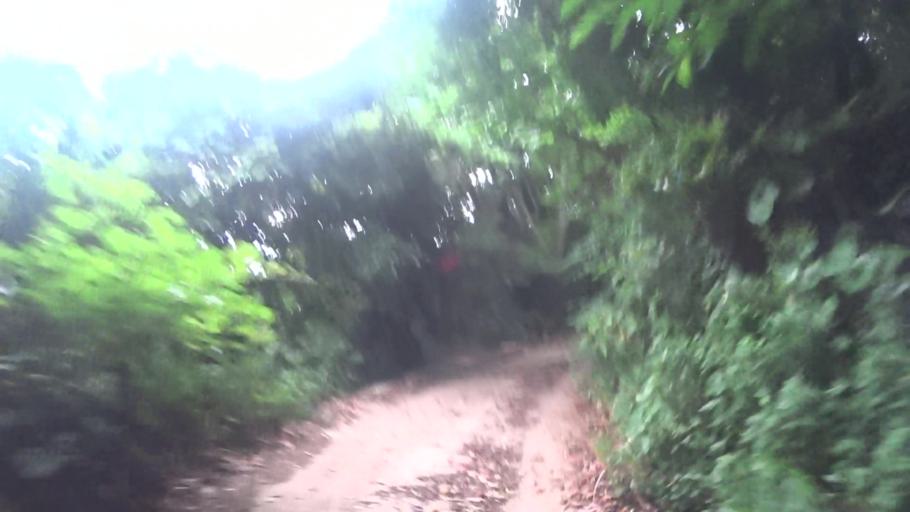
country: JP
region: Nagasaki
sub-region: Hirado Shi
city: Hirado
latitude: 33.1842
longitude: 129.3573
